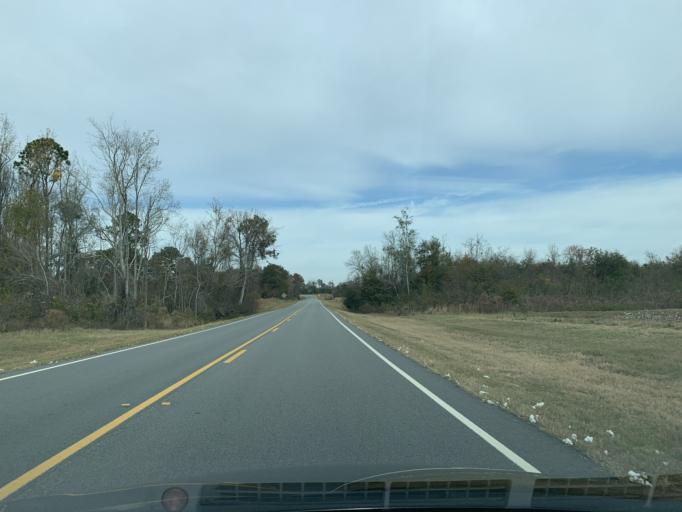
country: US
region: Georgia
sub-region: Wilcox County
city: Rochelle
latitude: 31.8396
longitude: -83.4280
